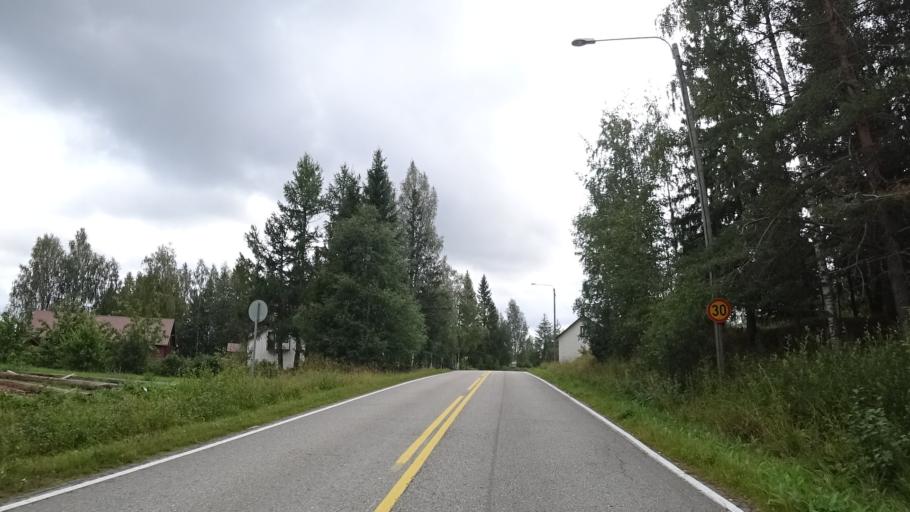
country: FI
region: North Karelia
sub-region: Joensuu
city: Ilomantsi
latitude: 62.9335
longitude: 31.2822
